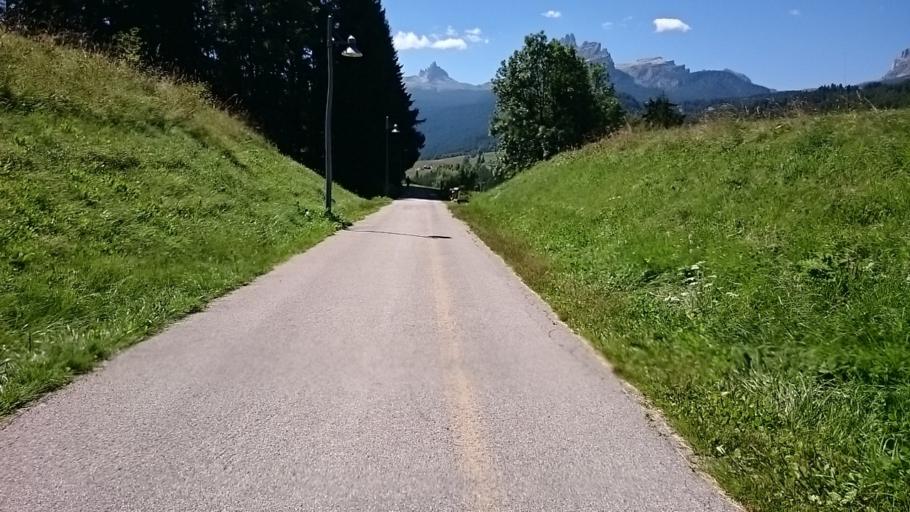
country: IT
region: Veneto
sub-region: Provincia di Belluno
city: Cortina d'Ampezzo
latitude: 46.5514
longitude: 12.1310
